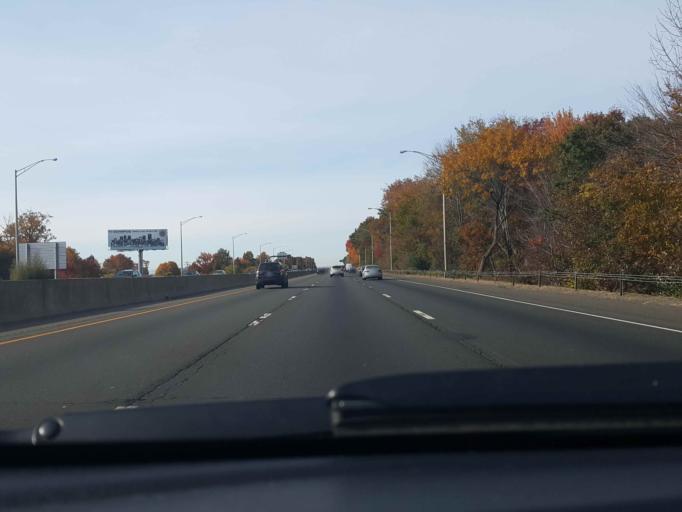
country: US
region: Connecticut
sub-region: New Haven County
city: West Haven
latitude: 41.2668
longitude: -72.9770
